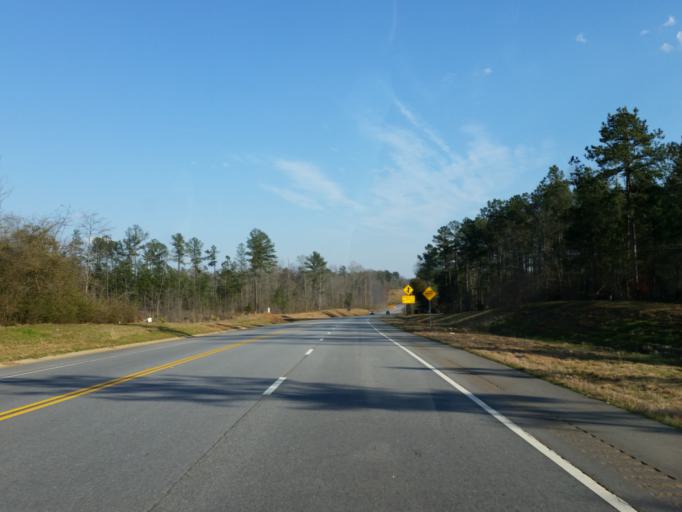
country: US
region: Georgia
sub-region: Monroe County
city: Forsyth
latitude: 33.0355
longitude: -83.9968
